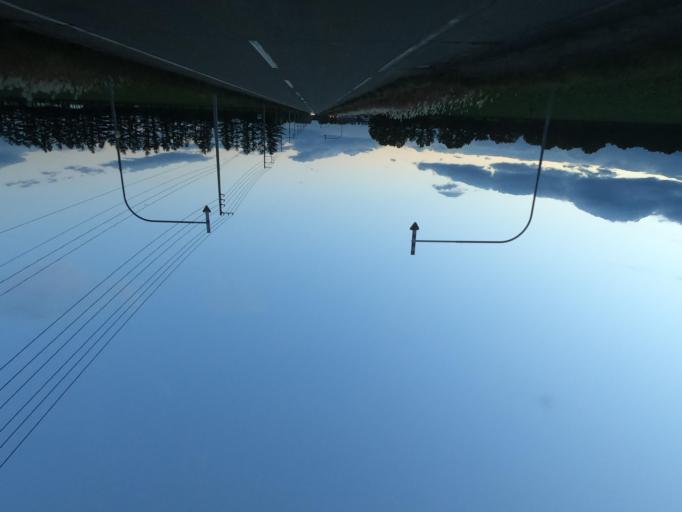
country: JP
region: Hokkaido
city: Obihiro
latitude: 42.6659
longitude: 143.1760
